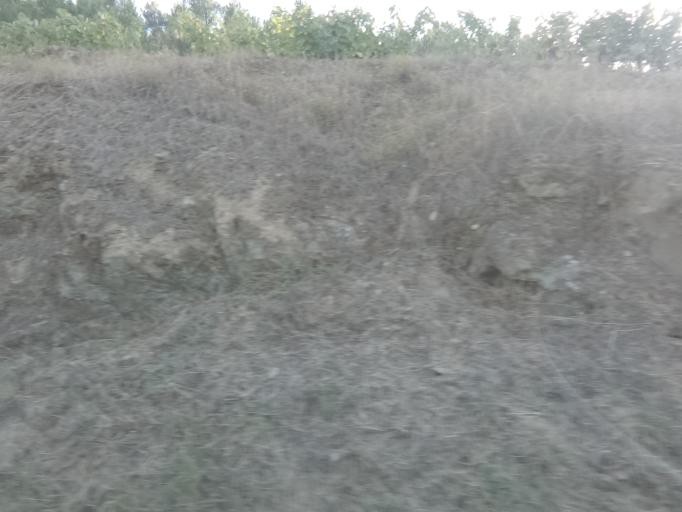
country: PT
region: Vila Real
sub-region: Sabrosa
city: Sabrosa
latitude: 41.2179
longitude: -7.5338
